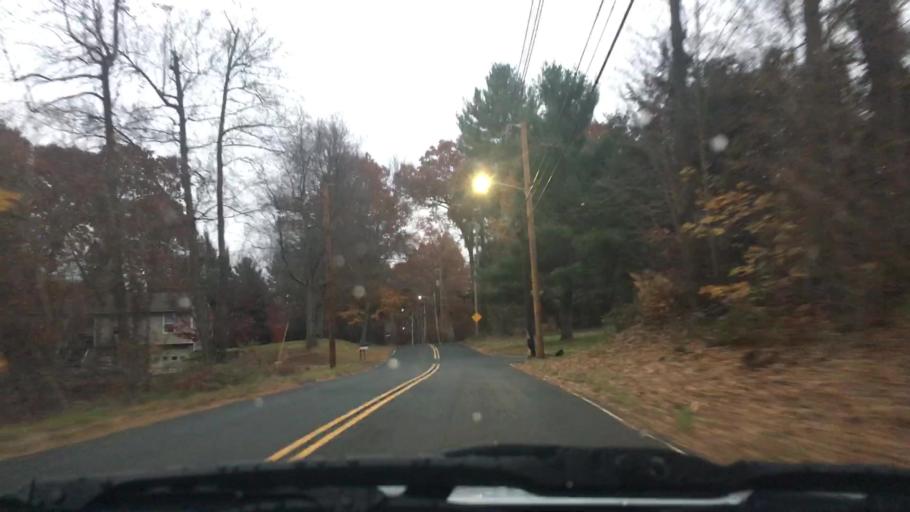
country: US
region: Massachusetts
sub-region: Hampden County
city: Westfield
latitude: 42.1169
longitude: -72.7873
